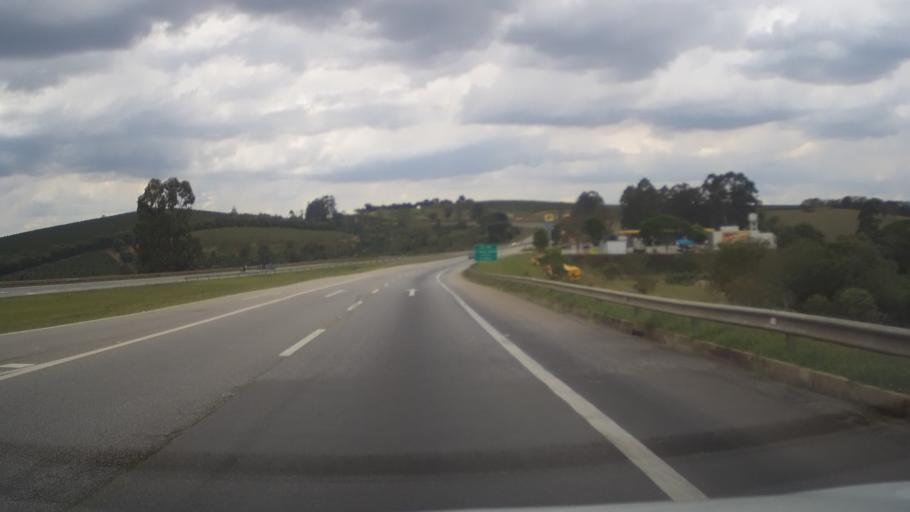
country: BR
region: Minas Gerais
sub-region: Tres Coracoes
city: Tres Coracoes
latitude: -21.4855
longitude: -45.2053
